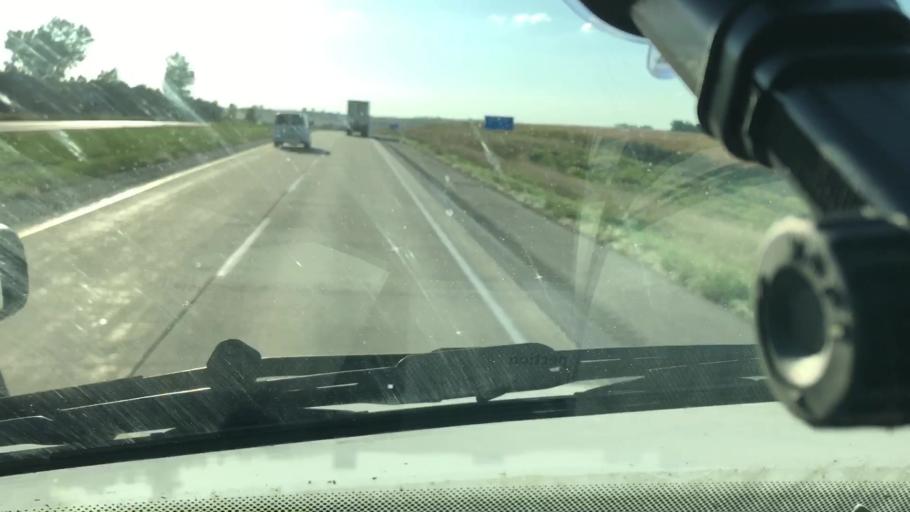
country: US
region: Iowa
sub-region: Pottawattamie County
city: Avoca
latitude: 41.4998
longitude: -95.5083
